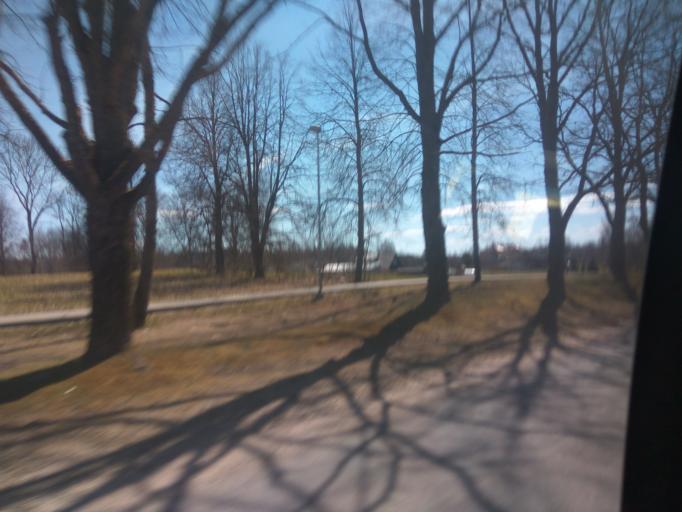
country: LV
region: Aluksnes Rajons
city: Aluksne
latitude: 57.4367
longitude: 27.0382
